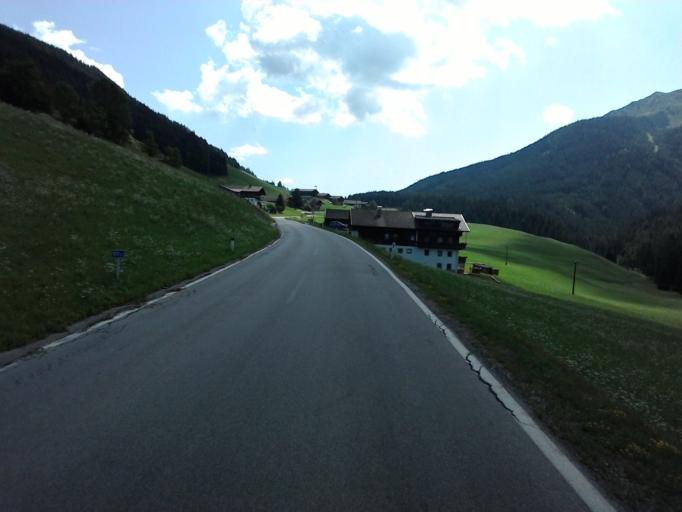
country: AT
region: Tyrol
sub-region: Politischer Bezirk Lienz
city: Kartitsch
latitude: 46.7222
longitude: 12.5126
